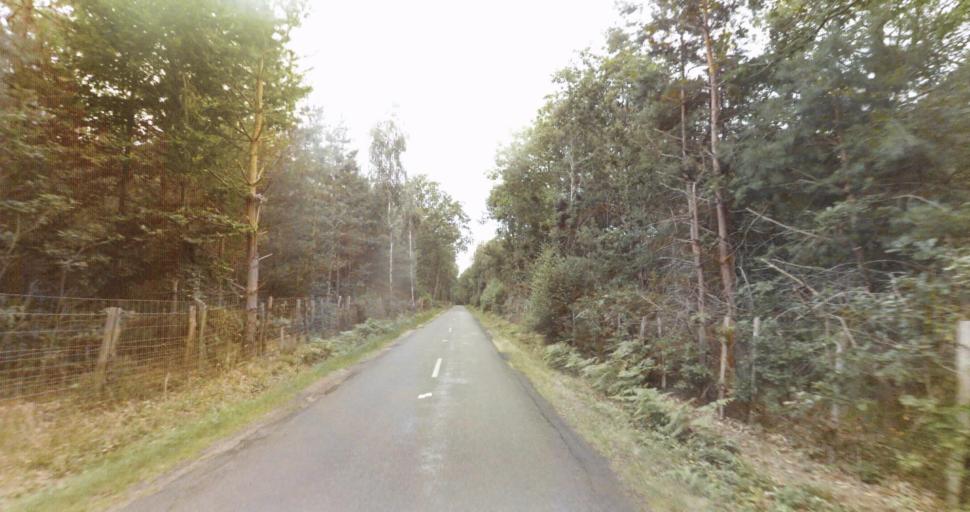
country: FR
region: Haute-Normandie
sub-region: Departement de l'Eure
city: Croth
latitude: 48.8576
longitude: 1.3603
